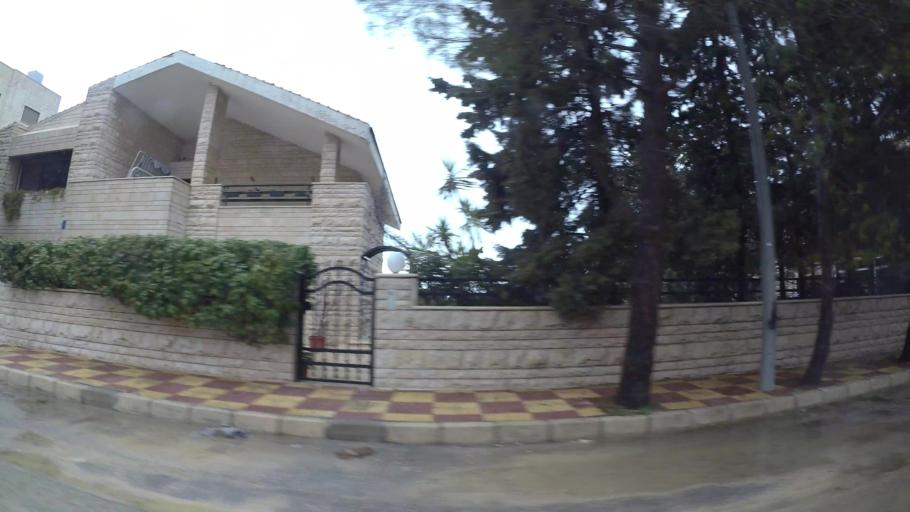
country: JO
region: Amman
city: Al Jubayhah
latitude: 32.0310
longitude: 35.8574
